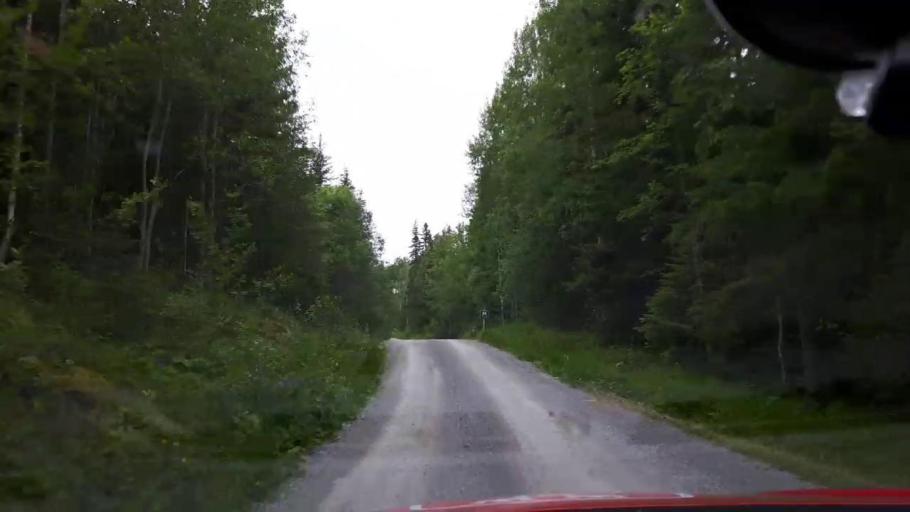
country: SE
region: Jaemtland
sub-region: OEstersunds Kommun
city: Brunflo
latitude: 63.0426
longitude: 14.9233
